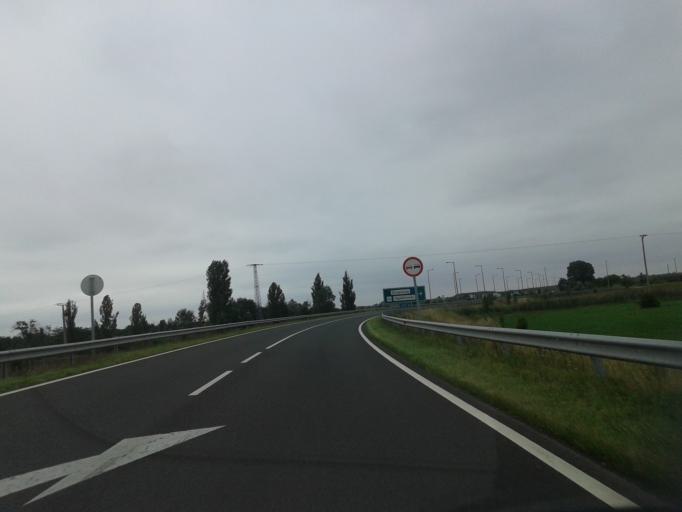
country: HU
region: Bacs-Kiskun
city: Dunavecse
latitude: 46.9048
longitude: 18.9905
